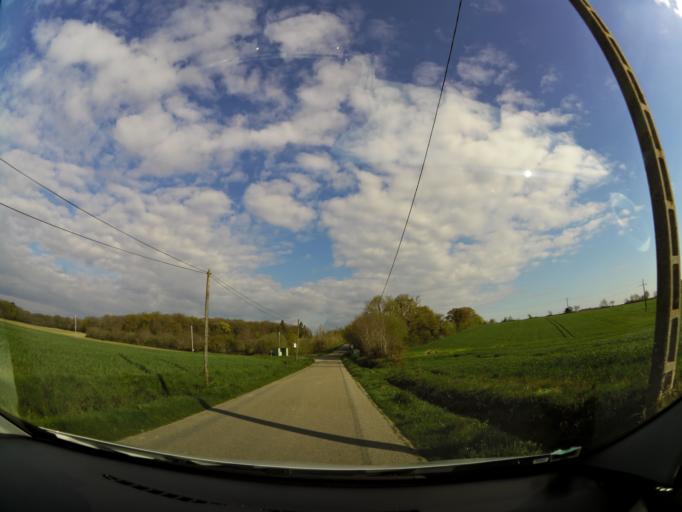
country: FR
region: Brittany
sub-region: Departement d'Ille-et-Vilaine
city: Laille
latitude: 47.9549
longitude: -1.7005
